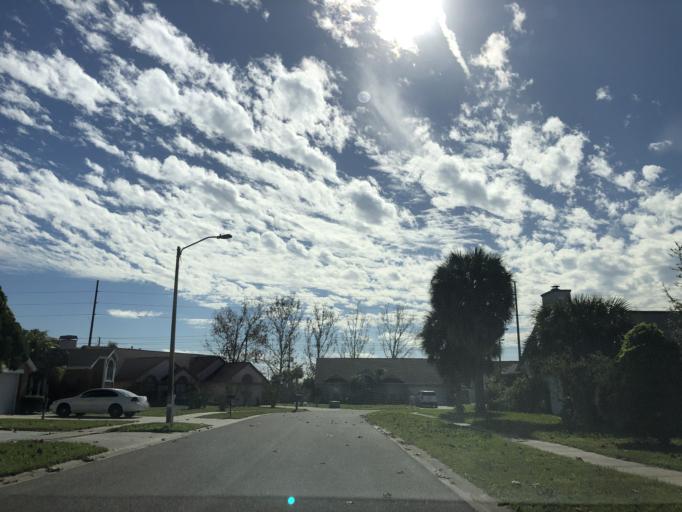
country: US
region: Florida
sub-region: Orange County
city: Hunters Creek
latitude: 28.3773
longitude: -81.4071
